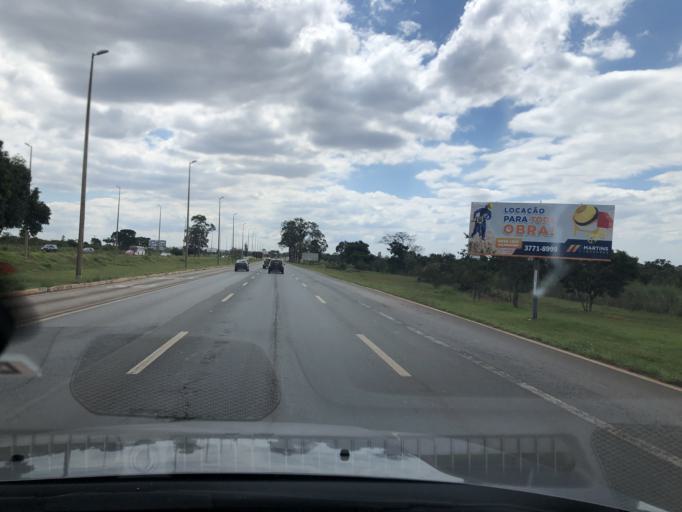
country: BR
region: Federal District
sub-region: Brasilia
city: Brasilia
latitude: -15.9591
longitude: -47.9933
